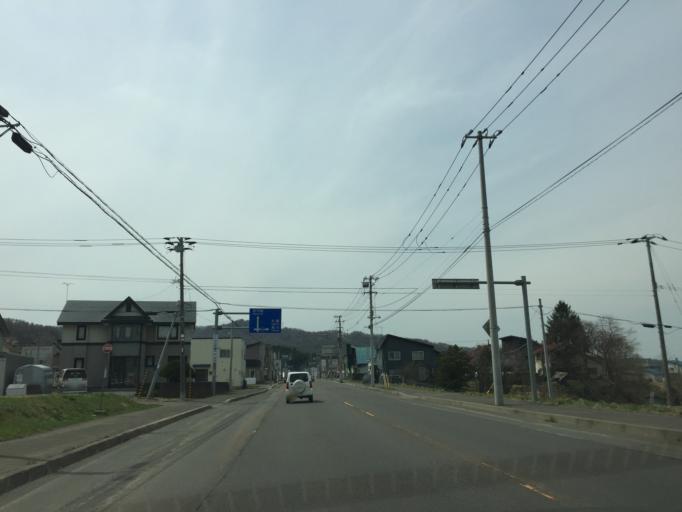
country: JP
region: Hokkaido
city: Akabira
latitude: 43.5393
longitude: 142.0872
